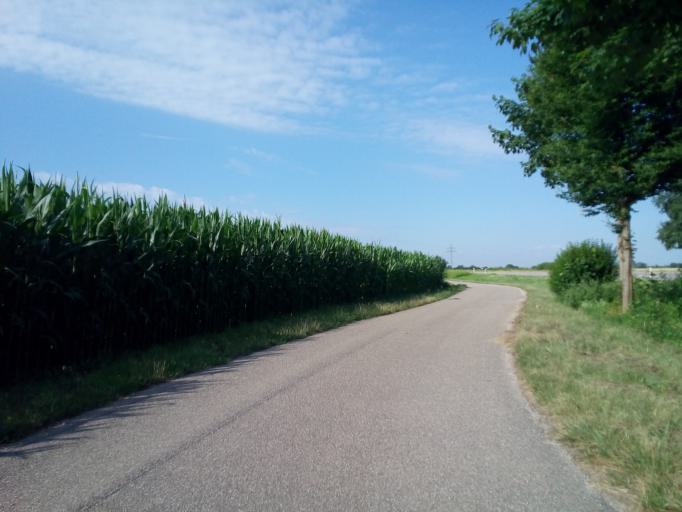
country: DE
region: Baden-Wuerttemberg
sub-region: Freiburg Region
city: Rheinau
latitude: 48.6792
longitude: 7.9648
